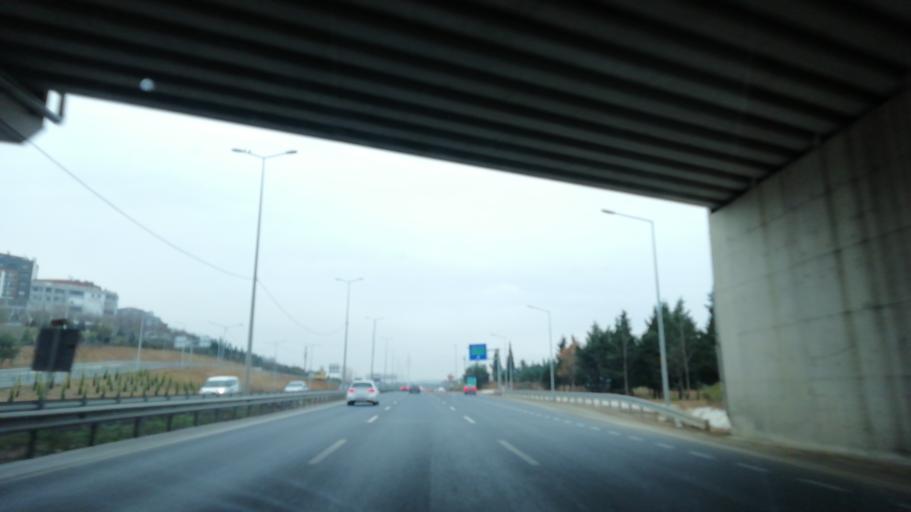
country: TR
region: Kocaeli
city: Darica
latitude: 40.8148
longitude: 29.3643
